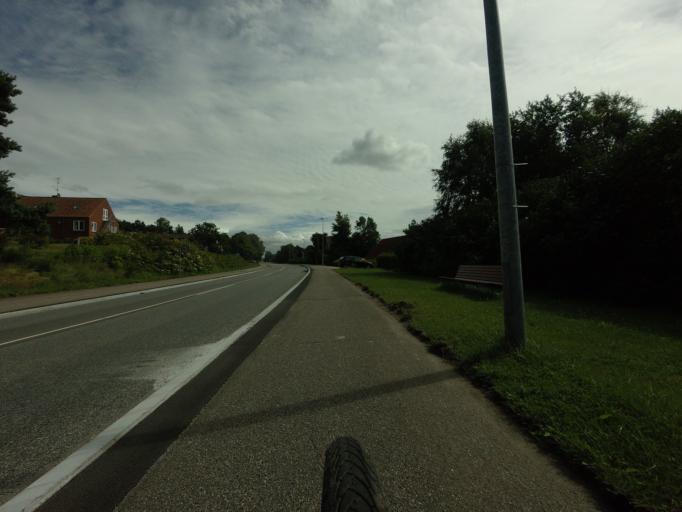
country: DK
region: Central Jutland
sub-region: Syddjurs Kommune
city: Ryomgard
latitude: 56.3829
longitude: 10.4801
